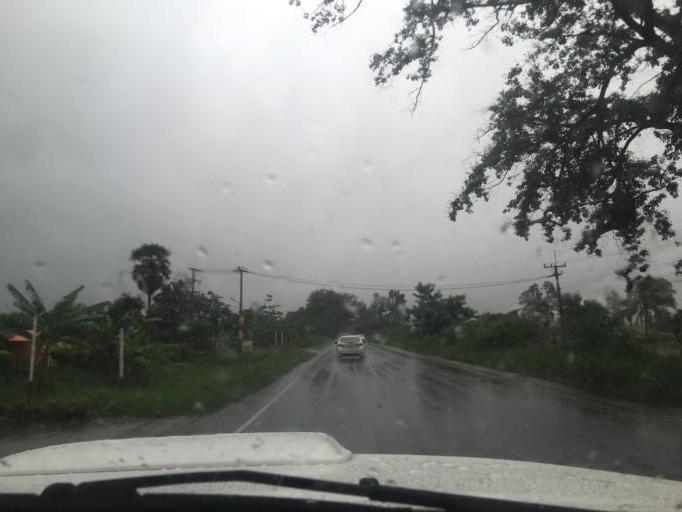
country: TH
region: Changwat Udon Thani
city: Udon Thani
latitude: 17.2965
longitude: 102.7037
